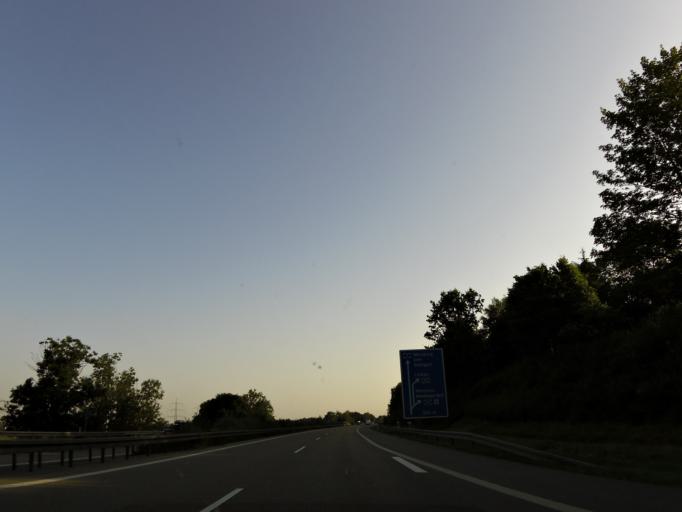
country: DE
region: Bavaria
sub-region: Swabia
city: Buxheim
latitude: 47.9865
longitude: 10.1507
